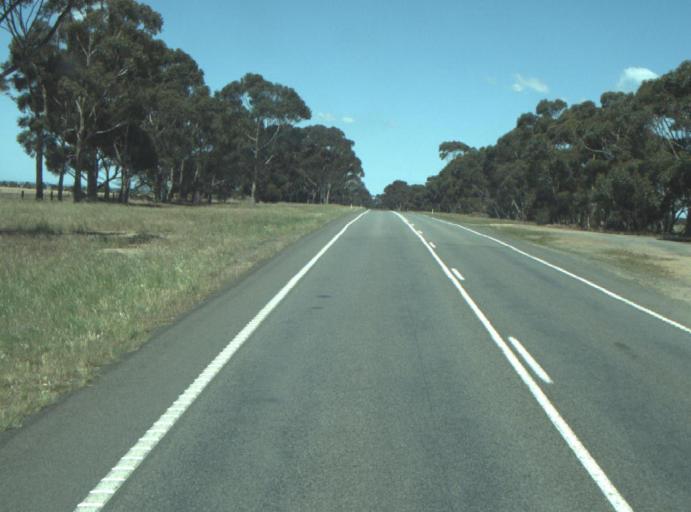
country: AU
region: Victoria
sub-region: Greater Geelong
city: Lara
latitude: -37.9293
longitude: 144.3617
